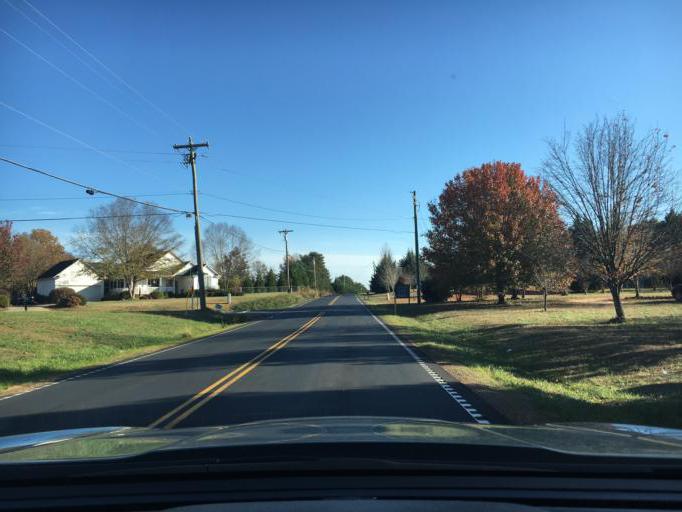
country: US
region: South Carolina
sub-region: Spartanburg County
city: Inman
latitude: 35.0214
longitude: -82.0830
